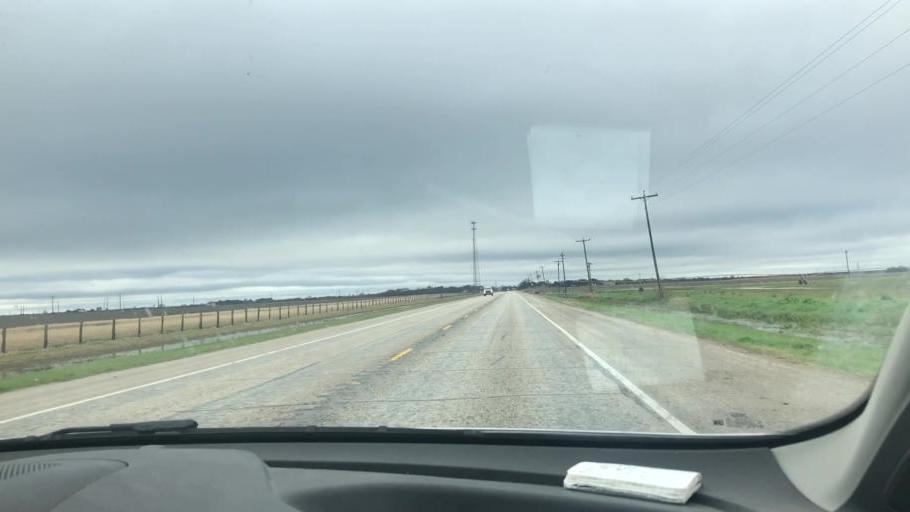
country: US
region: Texas
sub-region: Wharton County
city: Boling
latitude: 29.2355
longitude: -96.0385
